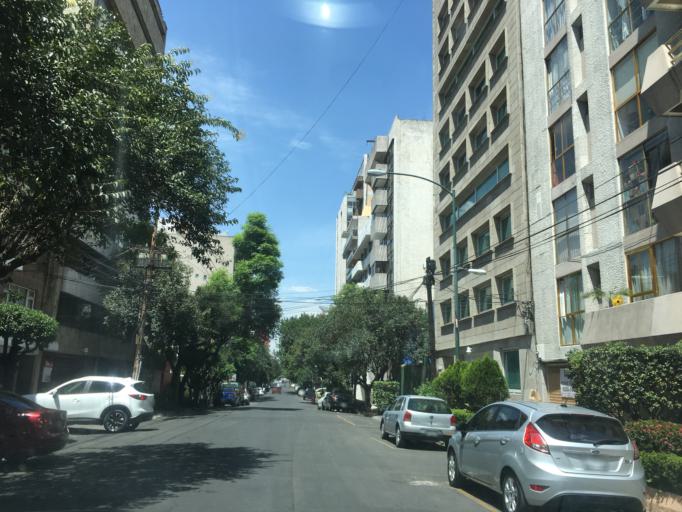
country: MX
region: Mexico City
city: Colonia del Valle
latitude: 19.3939
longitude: -99.1706
